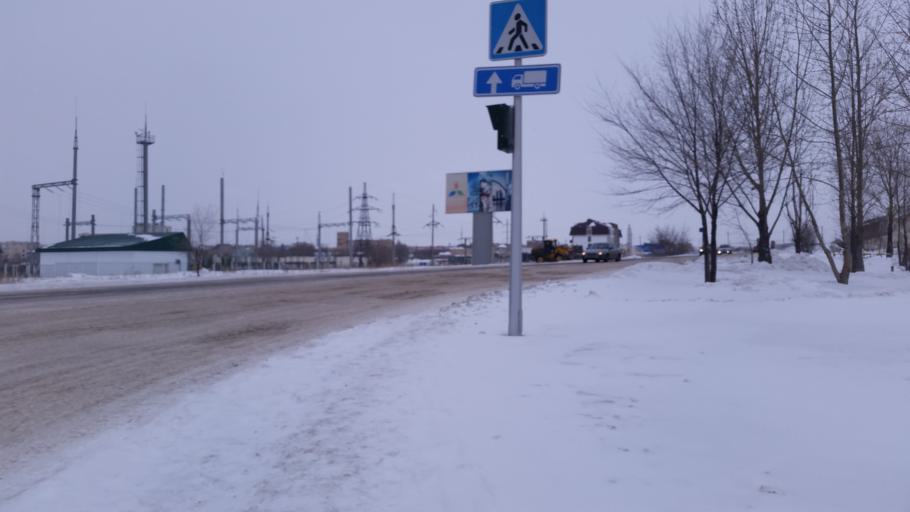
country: KZ
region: Qaraghandy
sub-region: Qaraghandy Qalasy
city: Karagandy
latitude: 49.7753
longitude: 73.1561
